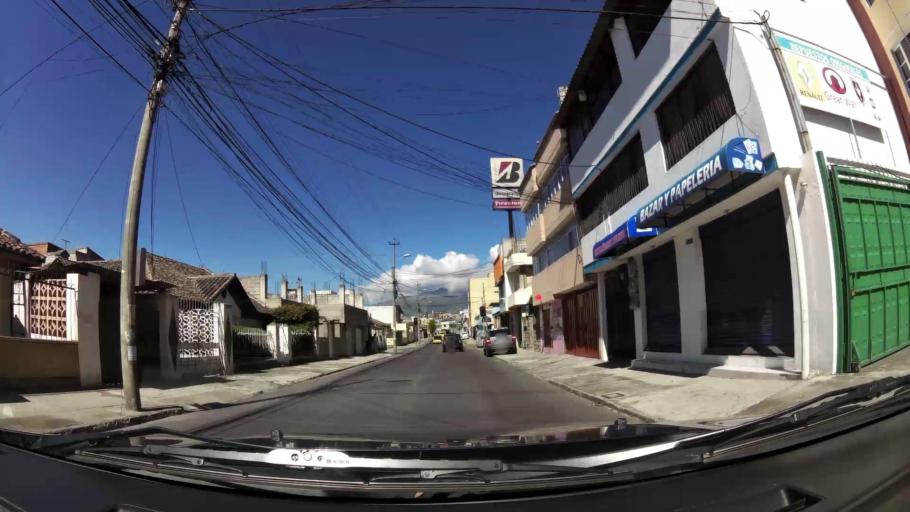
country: EC
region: Pichincha
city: Quito
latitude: -0.2439
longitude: -78.5276
